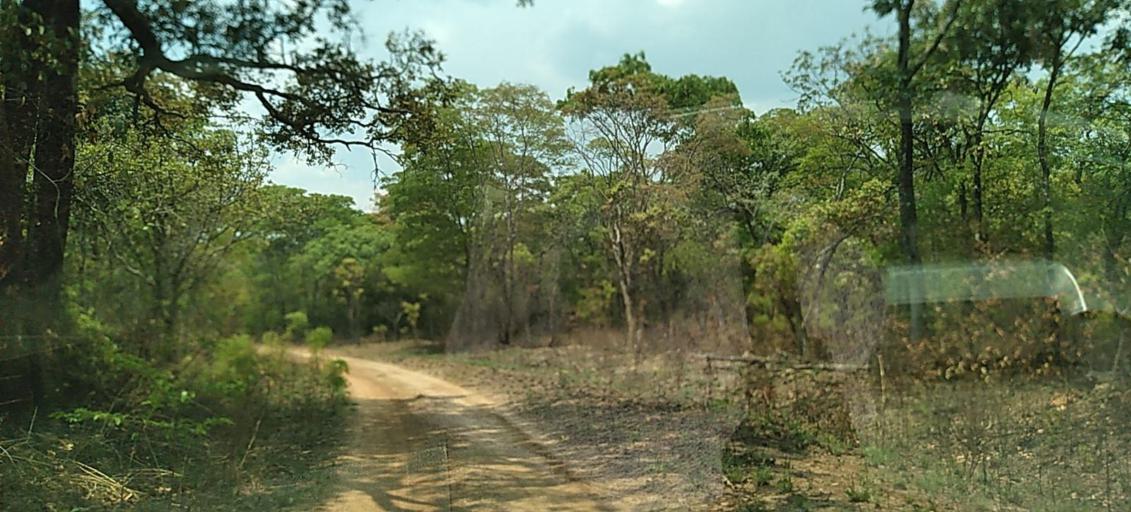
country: ZM
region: Copperbelt
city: Chingola
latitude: -12.7894
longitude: 27.6589
